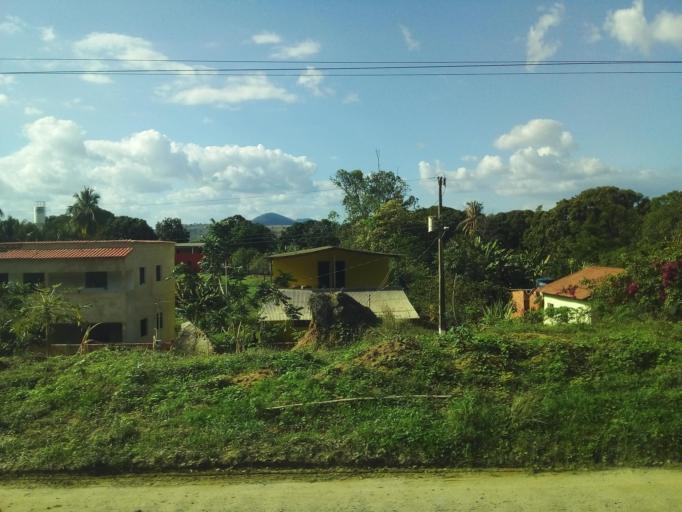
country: BR
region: Minas Gerais
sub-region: Conselheiro Pena
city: Conselheiro Pena
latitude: -19.0126
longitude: -41.5464
